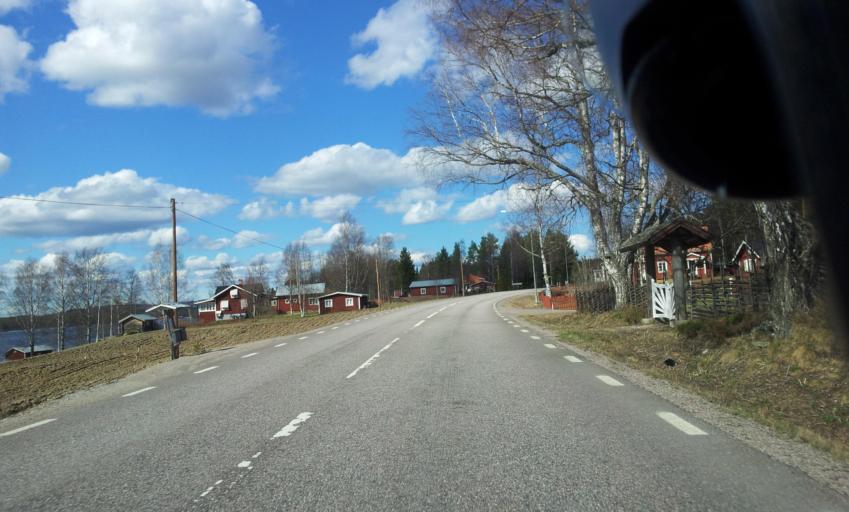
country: SE
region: Gaevleborg
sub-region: Ovanakers Kommun
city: Edsbyn
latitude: 61.2031
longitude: 15.8725
